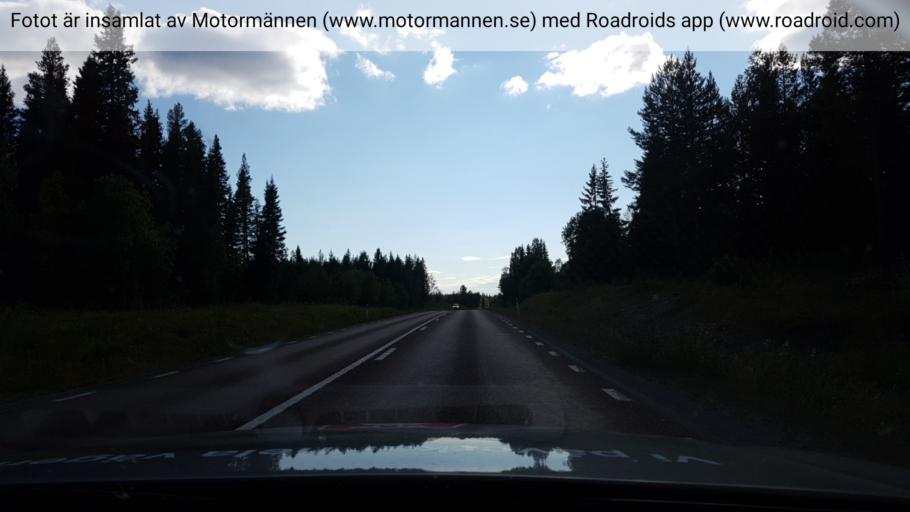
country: SE
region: Jaemtland
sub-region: OEstersunds Kommun
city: Brunflo
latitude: 63.0075
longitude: 14.6934
